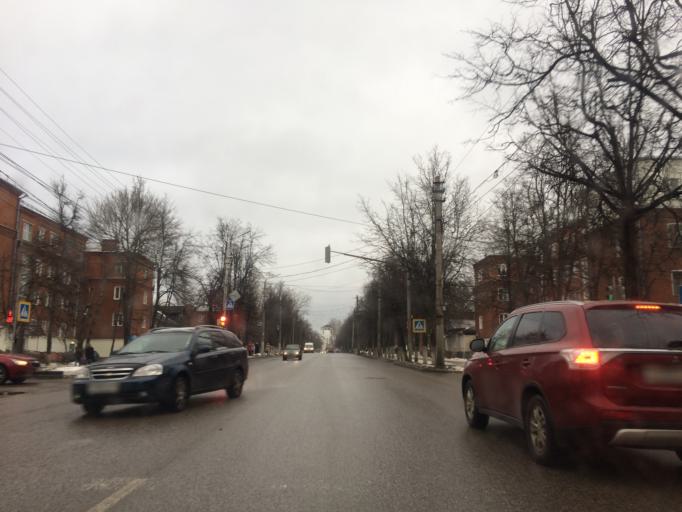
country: RU
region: Tula
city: Tula
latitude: 54.2080
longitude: 37.6578
